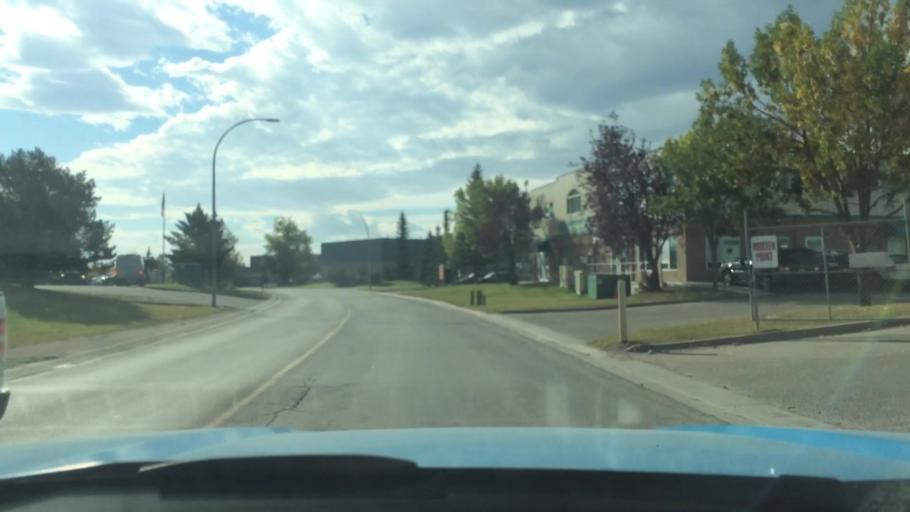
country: CA
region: Alberta
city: Calgary
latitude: 51.0109
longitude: -114.0353
